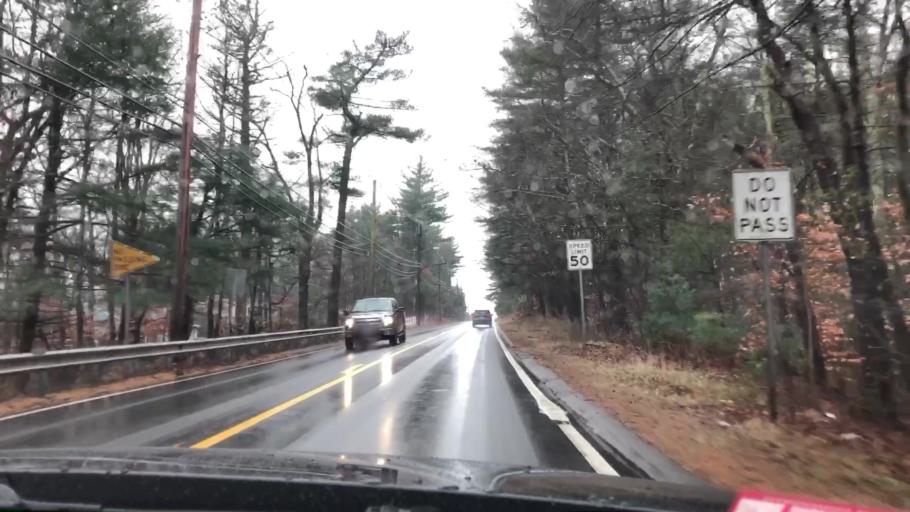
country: US
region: Massachusetts
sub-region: Norfolk County
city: Norfolk
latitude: 42.1093
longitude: -71.2854
